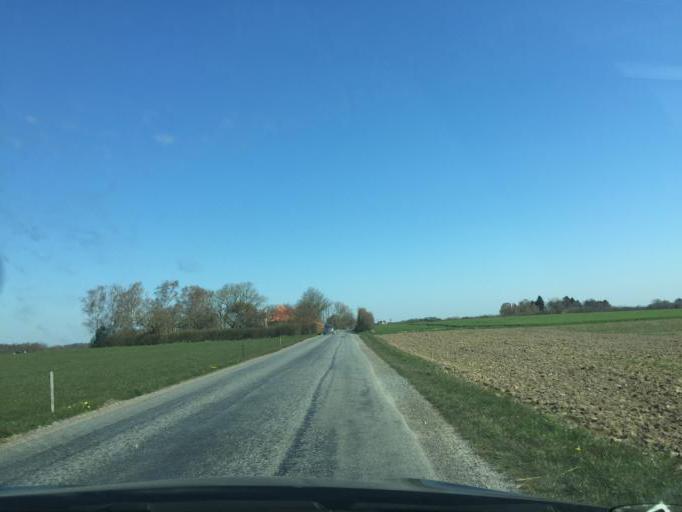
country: DK
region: South Denmark
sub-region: Faaborg-Midtfyn Kommune
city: Ringe
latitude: 55.2662
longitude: 10.5251
